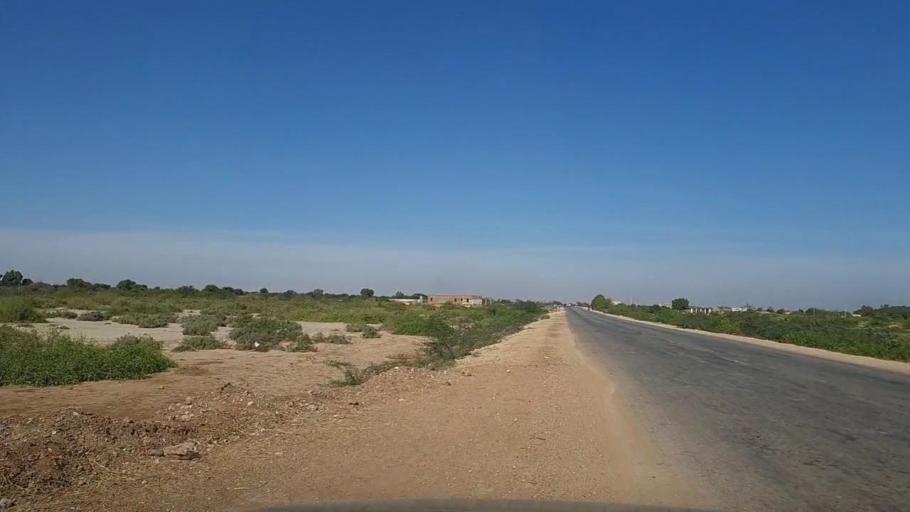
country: PK
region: Sindh
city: Kotri
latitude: 25.2185
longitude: 68.2377
